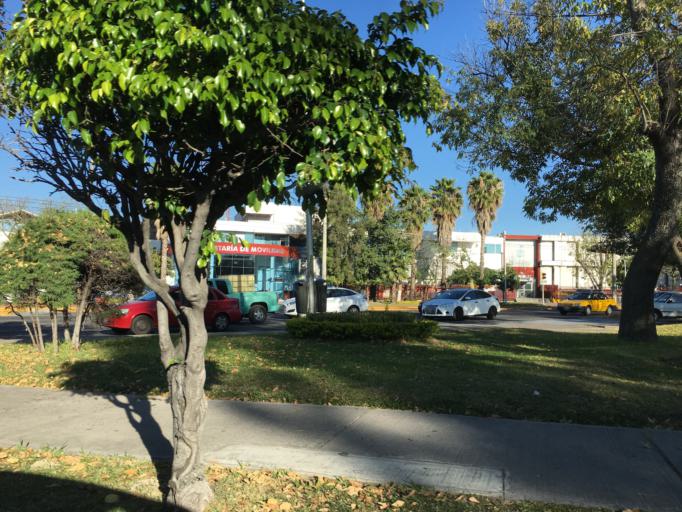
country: MX
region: Jalisco
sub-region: Zapopan
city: Zapopan
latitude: 20.7053
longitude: -103.3470
